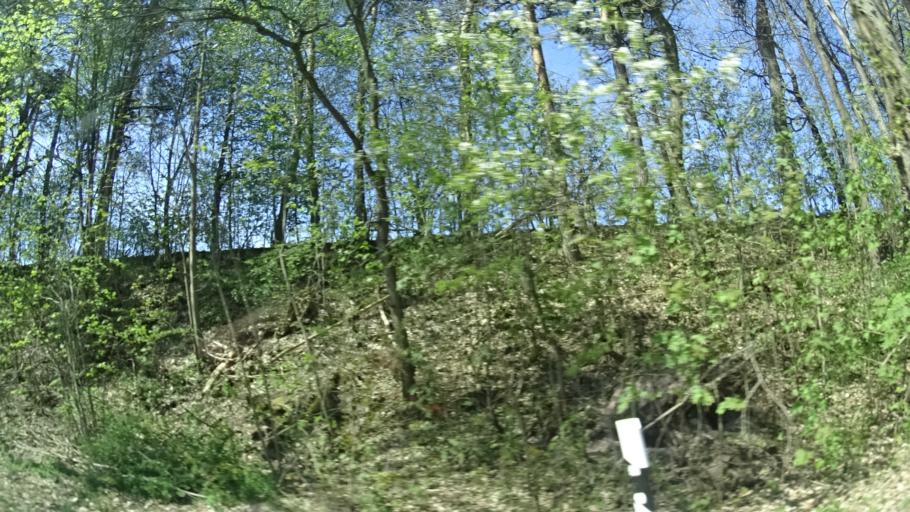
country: DE
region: Thuringia
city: Schleusingen
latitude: 50.4702
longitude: 10.7879
